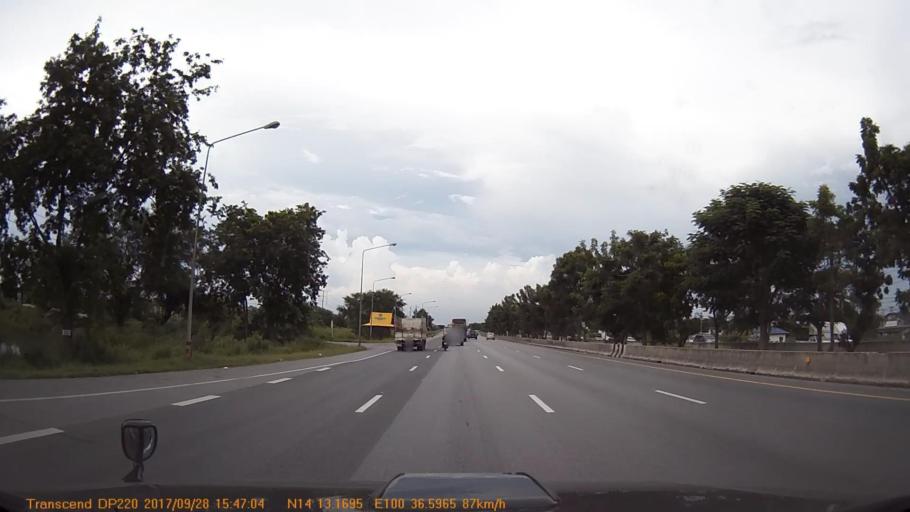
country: TH
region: Phra Nakhon Si Ayutthaya
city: Bang Pa-in
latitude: 14.2197
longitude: 100.6100
